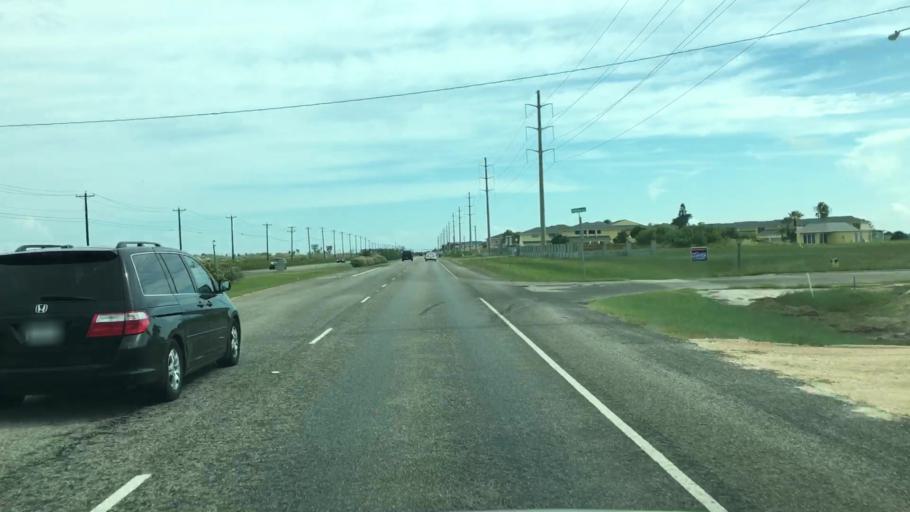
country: US
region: Texas
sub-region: Nueces County
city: Corpus Christi
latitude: 27.6147
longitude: -97.2223
